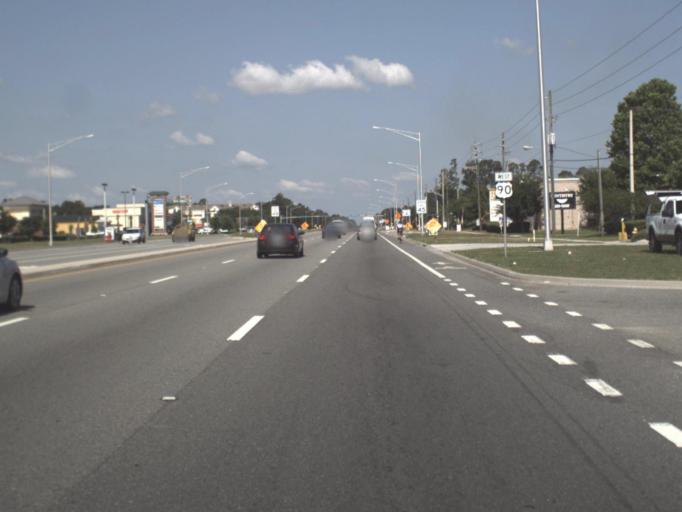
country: US
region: Florida
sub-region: Duval County
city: Jacksonville Beach
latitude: 30.2878
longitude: -81.4595
